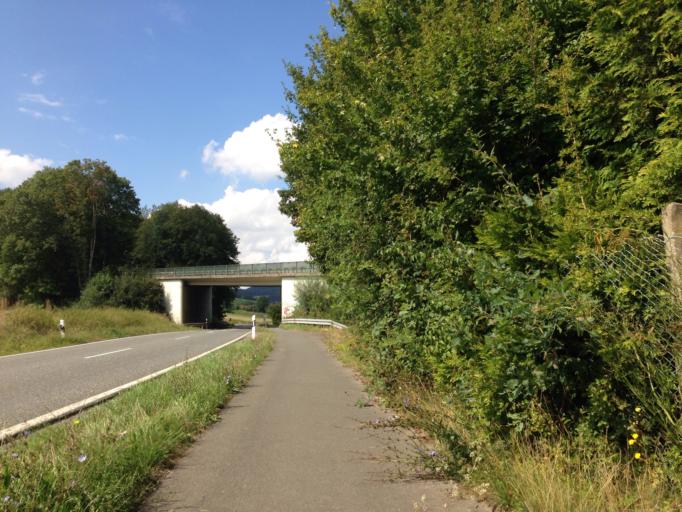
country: DE
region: Hesse
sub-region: Regierungsbezirk Giessen
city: Lohnberg
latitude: 50.5164
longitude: 8.2632
